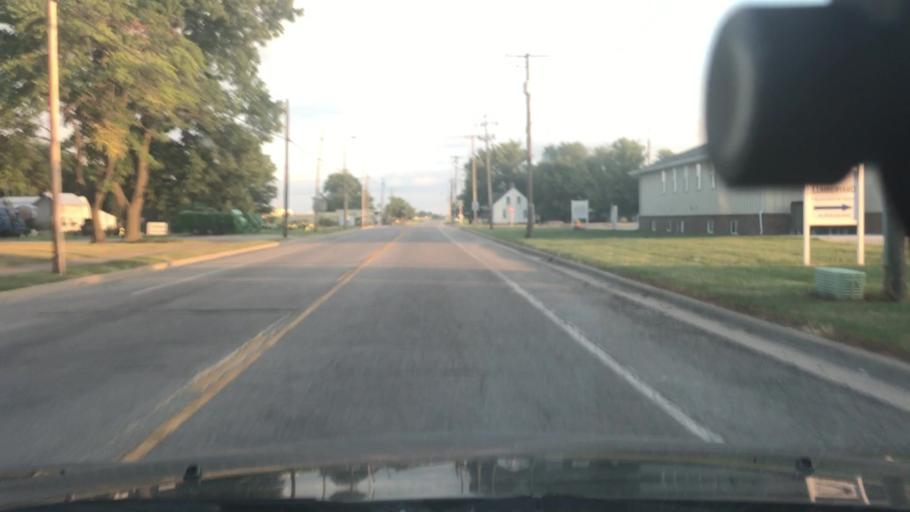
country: US
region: Illinois
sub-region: Washington County
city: Okawville
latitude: 38.4237
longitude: -89.5506
